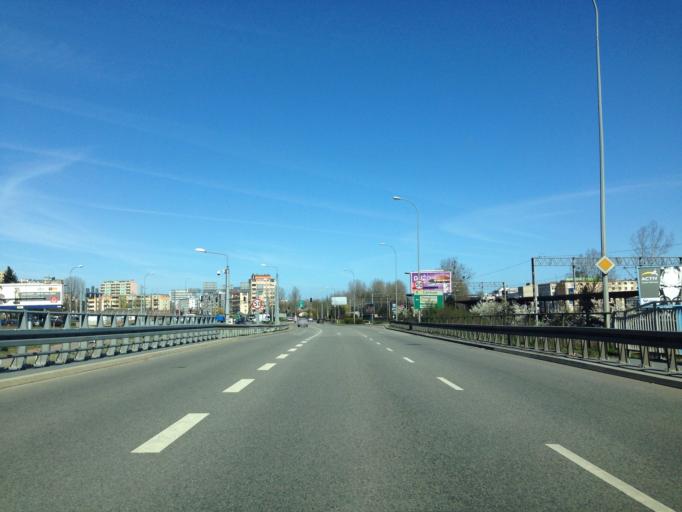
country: PL
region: Pomeranian Voivodeship
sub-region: Gdynia
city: Gdynia
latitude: 54.5065
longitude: 18.5345
